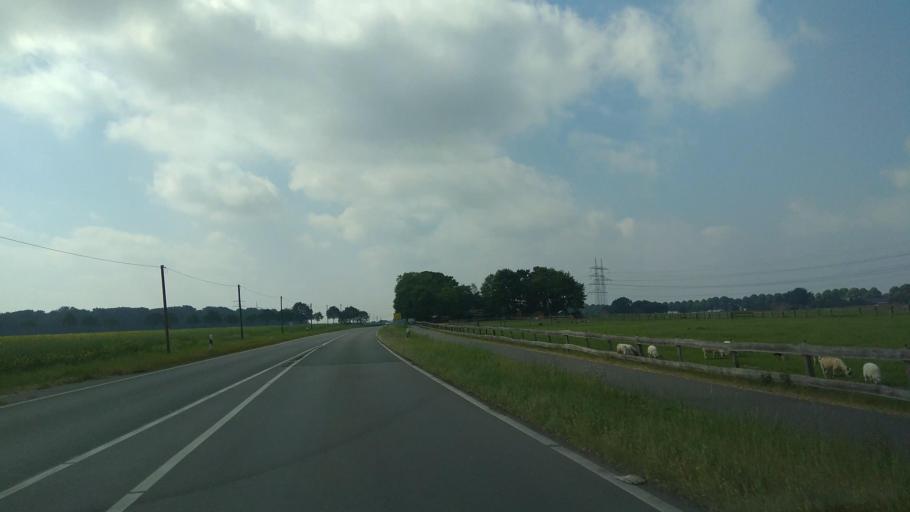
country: DE
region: North Rhine-Westphalia
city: Marl
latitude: 51.6275
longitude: 7.0862
